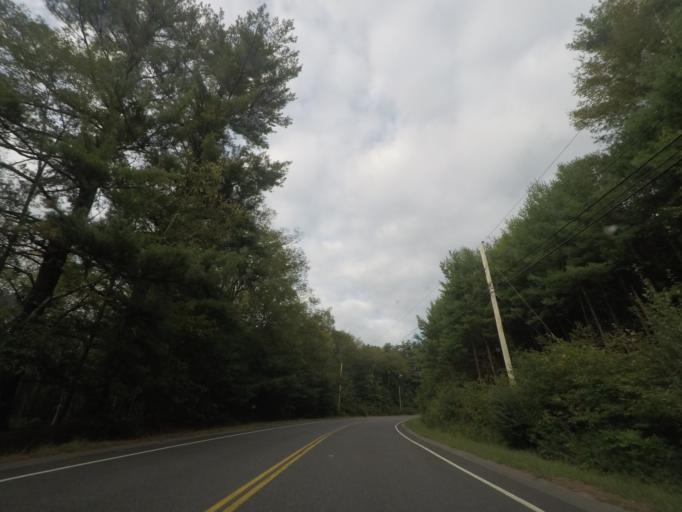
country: US
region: Massachusetts
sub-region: Hampden County
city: Palmer
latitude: 42.1883
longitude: -72.2971
